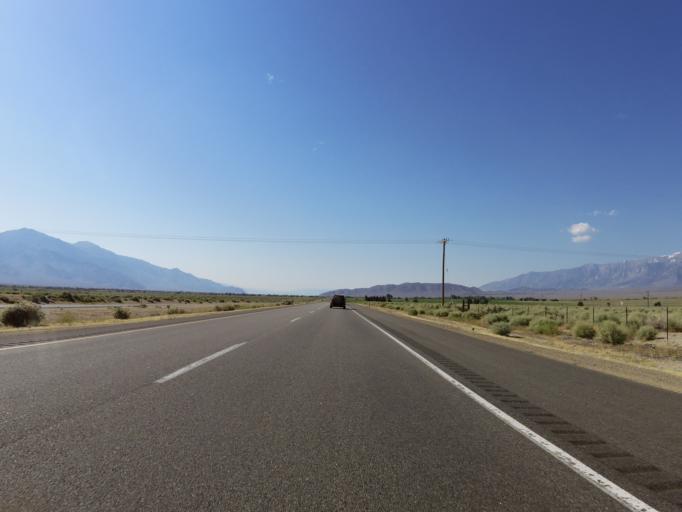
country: US
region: California
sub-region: Inyo County
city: Lone Pine
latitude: 36.7613
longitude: -118.1700
